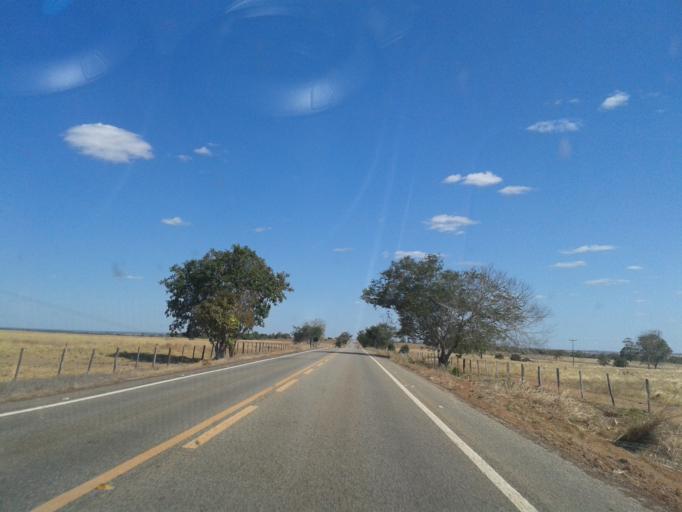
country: BR
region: Goias
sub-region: Sao Miguel Do Araguaia
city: Sao Miguel do Araguaia
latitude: -13.4051
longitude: -50.2616
